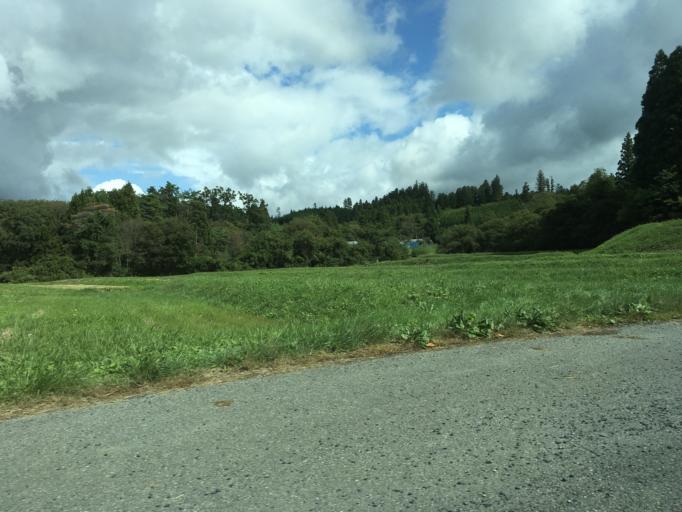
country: JP
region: Iwate
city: Ichinoseki
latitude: 38.8325
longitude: 141.3589
